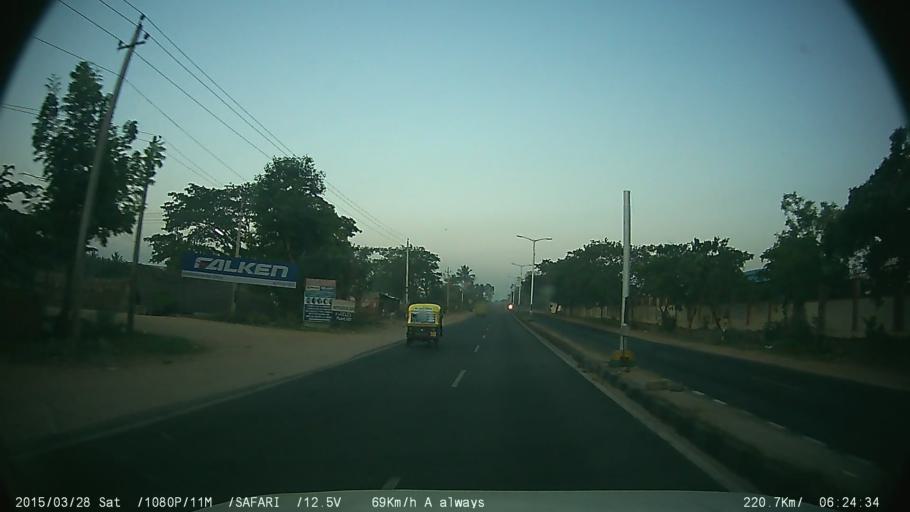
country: IN
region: Karnataka
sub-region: Ramanagara
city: Ramanagaram
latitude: 12.7122
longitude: 77.2708
